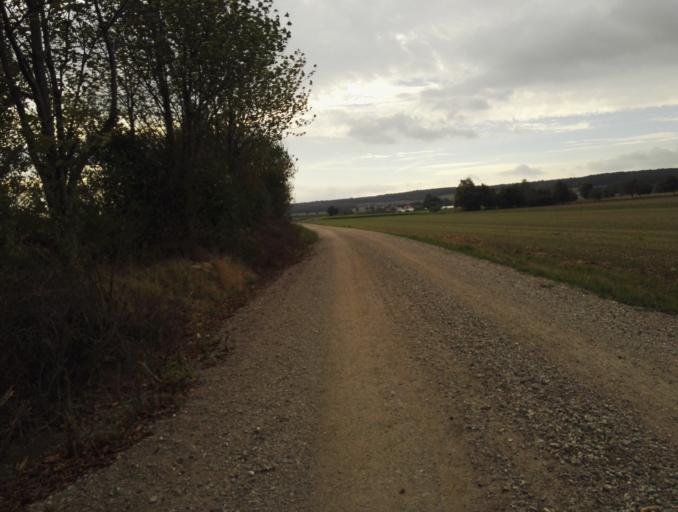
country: DE
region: Lower Saxony
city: Schellerten
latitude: 52.1477
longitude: 10.0584
